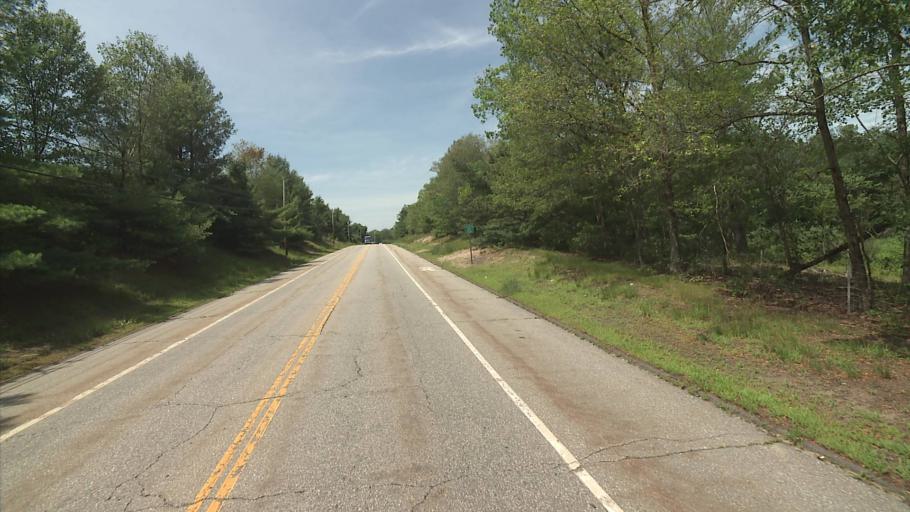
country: US
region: Connecticut
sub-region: Windham County
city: Willimantic
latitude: 41.7321
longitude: -72.2075
